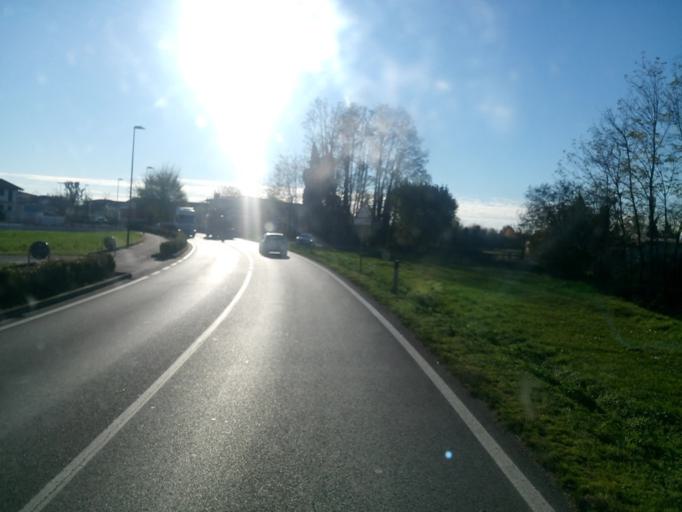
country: IT
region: Veneto
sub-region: Provincia di Vicenza
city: Rossano Veneto
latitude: 45.6977
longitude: 11.8280
